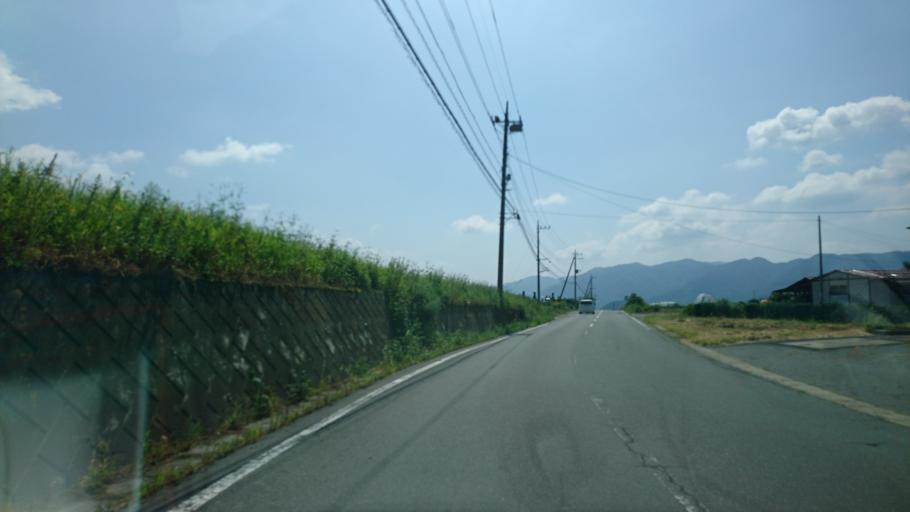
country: JP
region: Gunma
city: Numata
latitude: 36.7509
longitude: 139.2456
